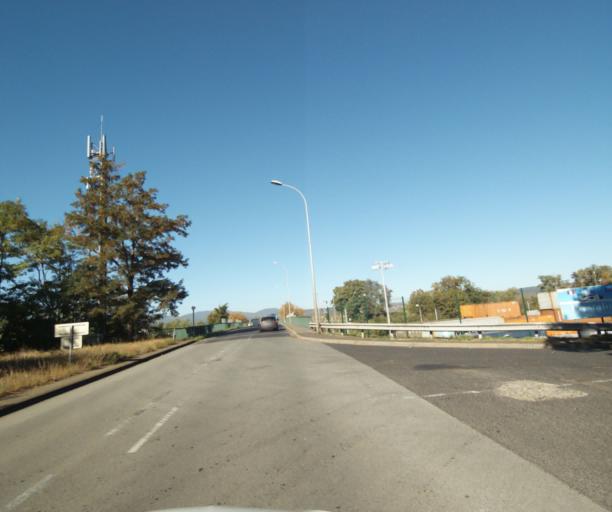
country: FR
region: Auvergne
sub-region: Departement du Puy-de-Dome
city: Gerzat
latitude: 45.8225
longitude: 3.1390
